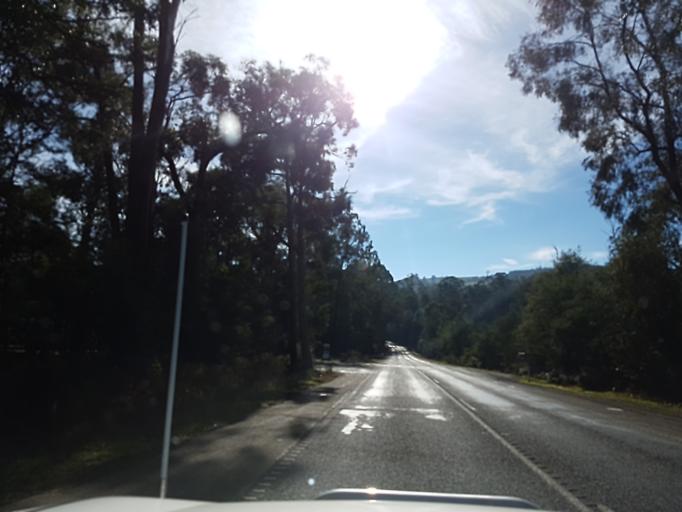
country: AU
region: Victoria
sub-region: Yarra Ranges
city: Yarra Glen
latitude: -37.5157
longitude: 145.4250
